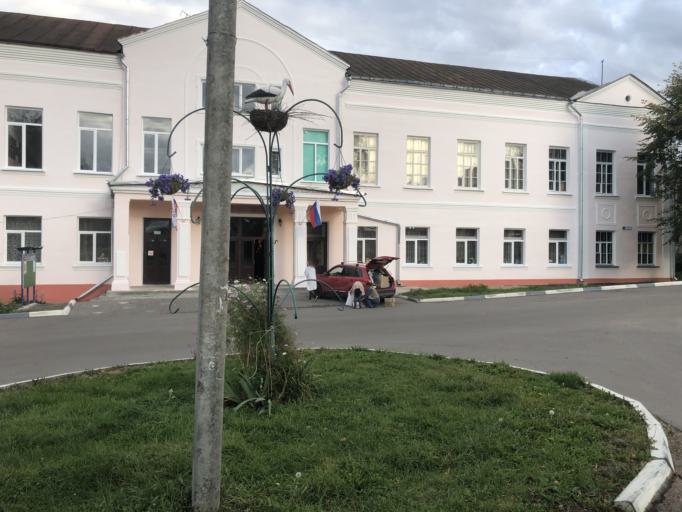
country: RU
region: Tverskaya
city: Rzhev
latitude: 56.2556
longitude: 34.2928
